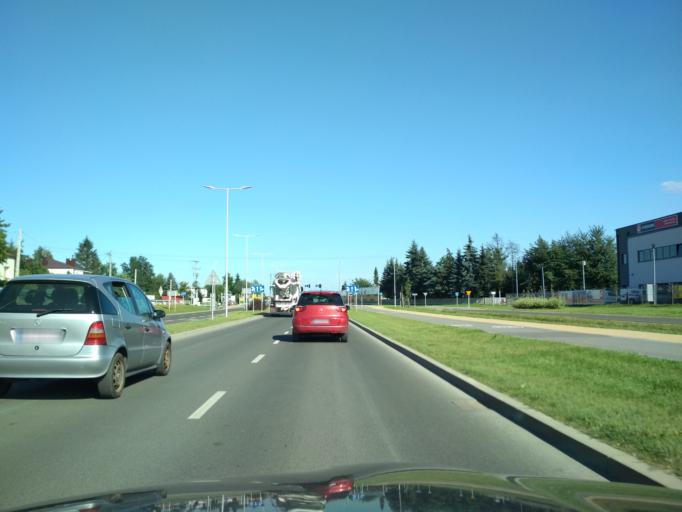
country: PL
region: Subcarpathian Voivodeship
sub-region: Powiat rzeszowski
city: Trzebownisko
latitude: 50.0562
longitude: 22.0302
